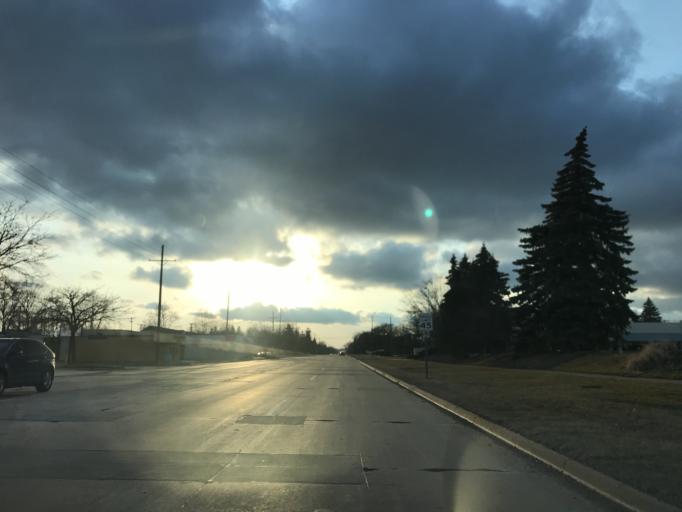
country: US
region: Michigan
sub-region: Oakland County
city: Farmington
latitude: 42.4262
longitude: -83.3768
